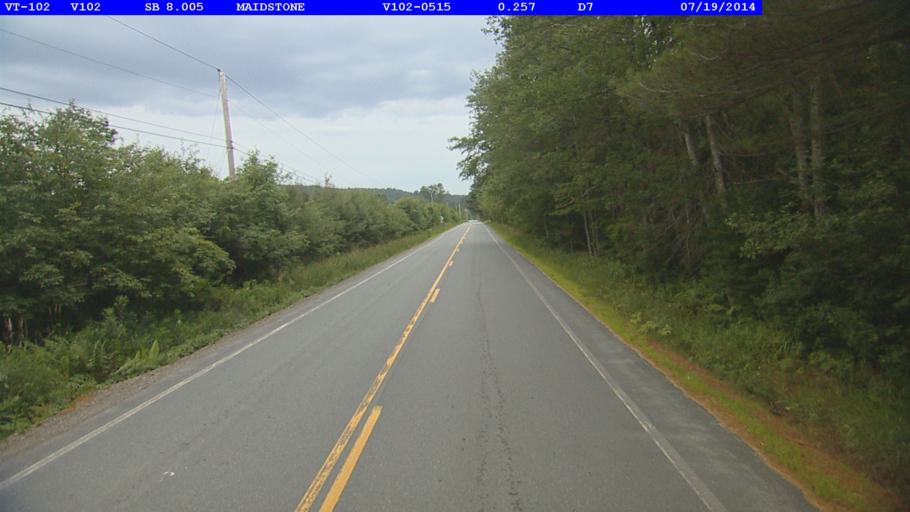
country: US
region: Vermont
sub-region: Essex County
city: Guildhall
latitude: 44.5746
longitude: -71.5547
